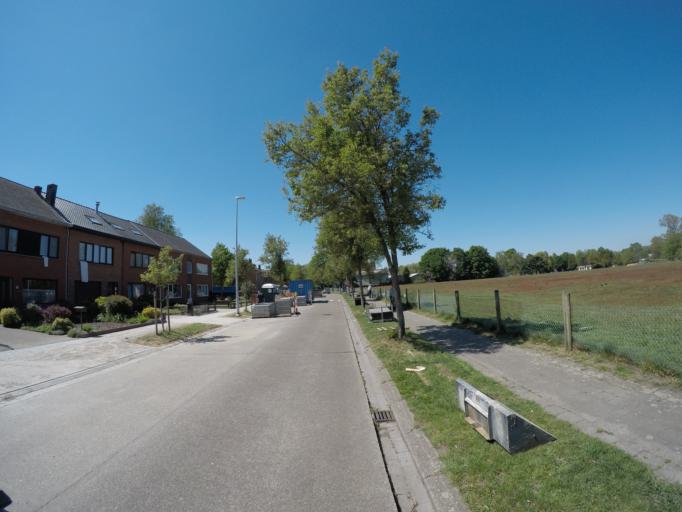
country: BE
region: Flanders
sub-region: Provincie Antwerpen
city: Schoten
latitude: 51.2482
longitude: 4.5093
